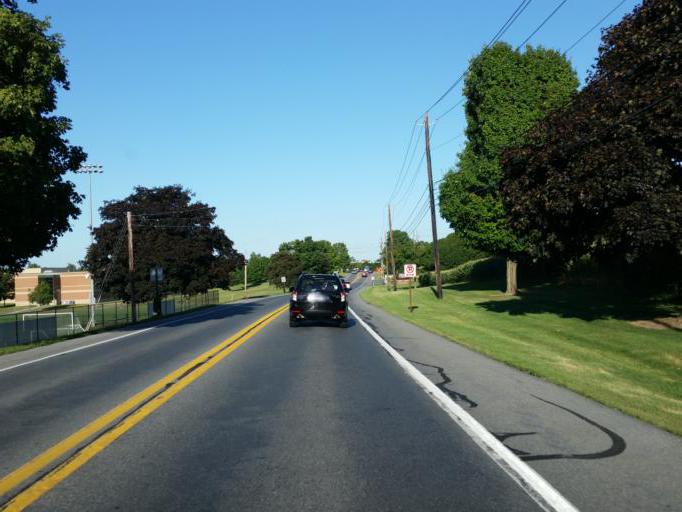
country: US
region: Pennsylvania
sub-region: Dauphin County
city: Hershey
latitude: 40.2751
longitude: -76.6447
